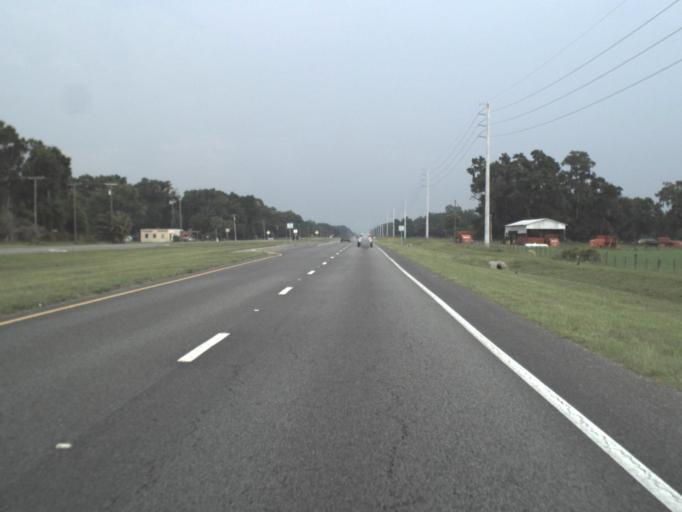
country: US
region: Florida
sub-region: Levy County
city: Chiefland
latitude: 29.4746
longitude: -82.8388
